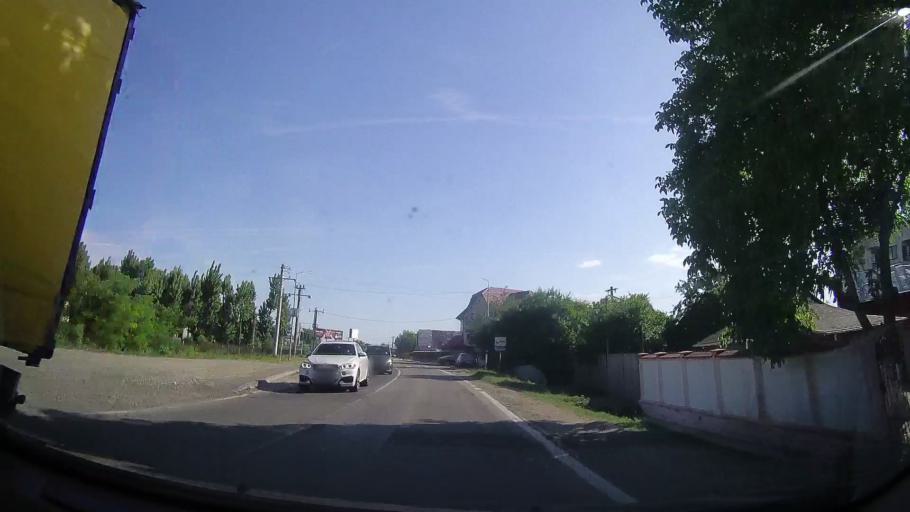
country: RO
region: Prahova
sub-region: Comuna Barcanesti
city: Barcanesti
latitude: 44.8885
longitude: 26.0464
